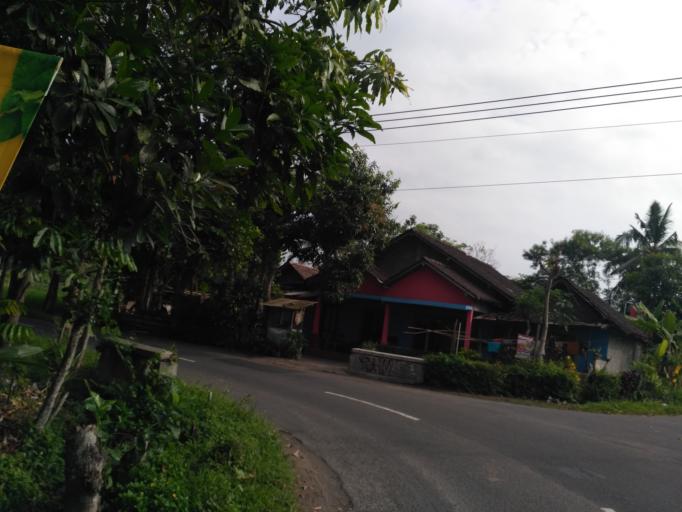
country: ID
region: Daerah Istimewa Yogyakarta
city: Melati
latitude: -7.7112
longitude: 110.3976
